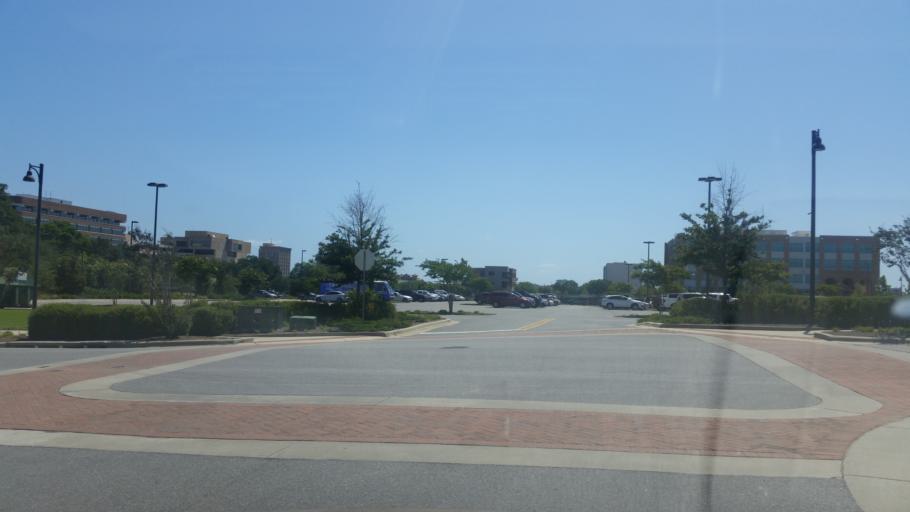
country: US
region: Florida
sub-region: Escambia County
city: Pensacola
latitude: 30.4056
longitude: -87.2206
